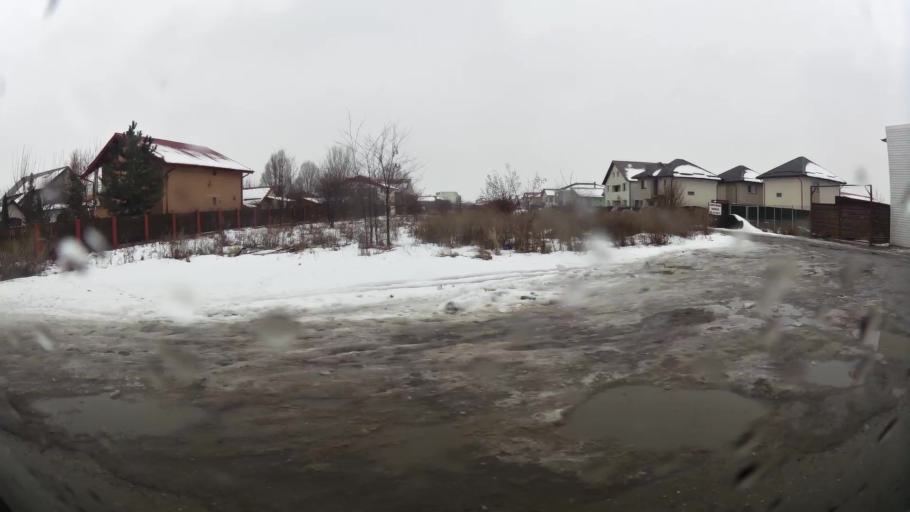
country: RO
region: Ilfov
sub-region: Comuna Bragadiru
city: Bragadiru
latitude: 44.3979
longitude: 26.0038
